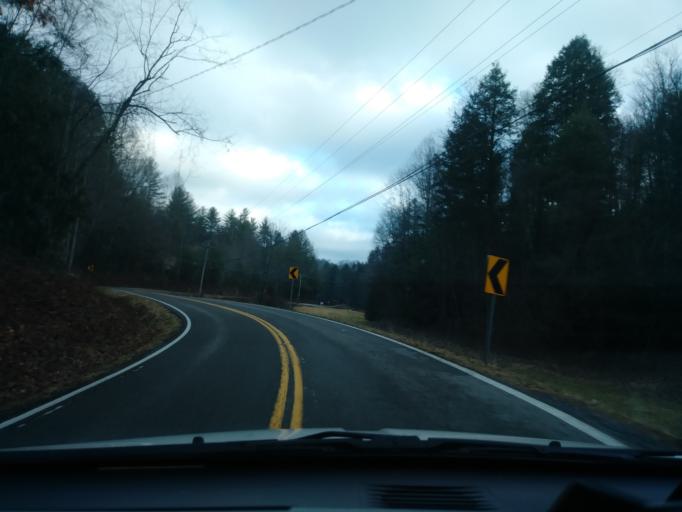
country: US
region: Tennessee
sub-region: Unicoi County
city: Unicoi
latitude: 36.2045
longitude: -82.2344
